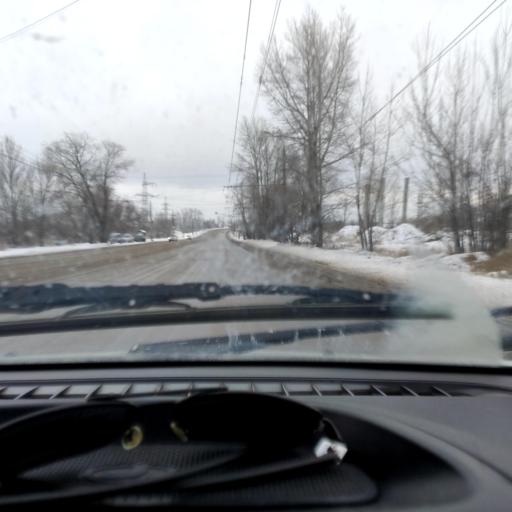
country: RU
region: Samara
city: Zhigulevsk
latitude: 53.4927
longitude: 49.5041
